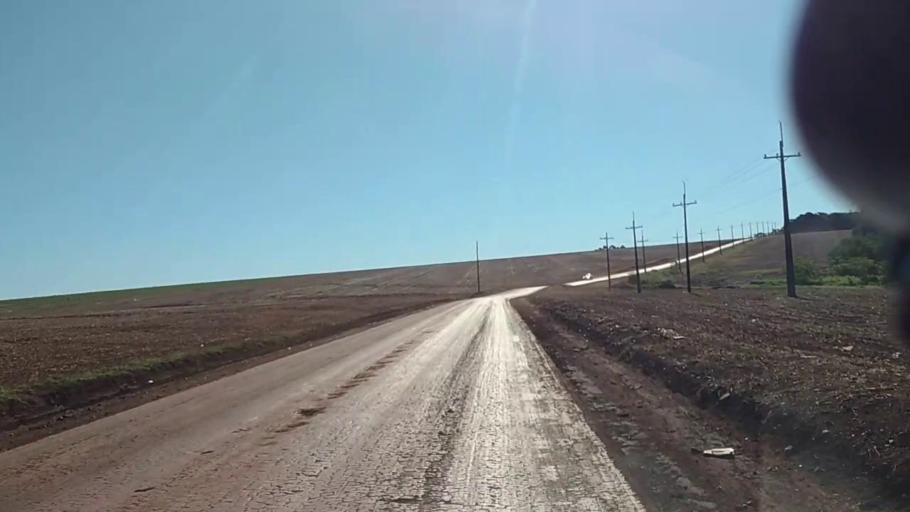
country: PY
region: Alto Parana
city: Naranjal
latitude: -25.9693
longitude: -55.2407
